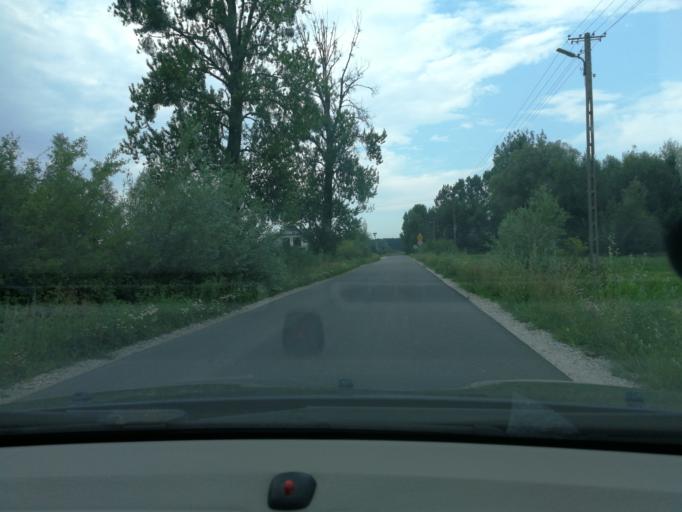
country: PL
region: Masovian Voivodeship
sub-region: Powiat warszawski zachodni
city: Bieniewice
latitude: 52.1109
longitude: 20.5541
